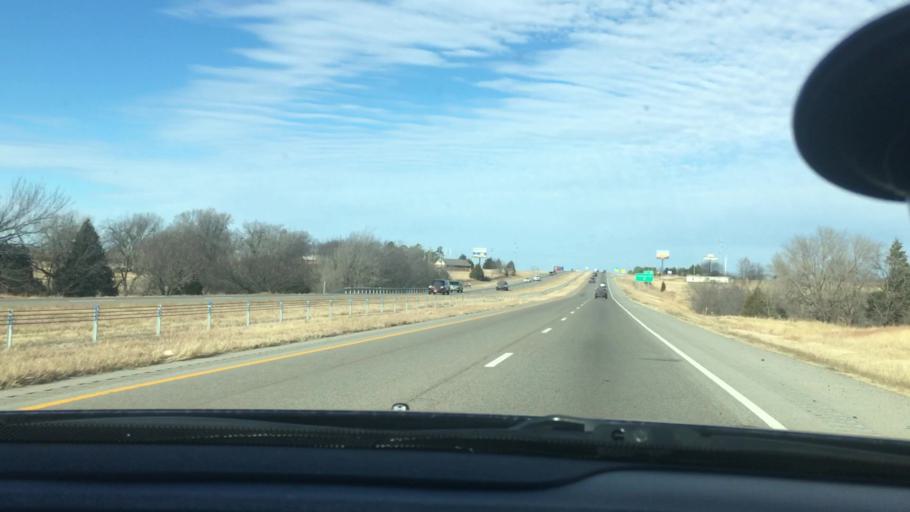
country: US
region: Oklahoma
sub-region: Cleveland County
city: Noble
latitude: 35.0737
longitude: -97.4024
